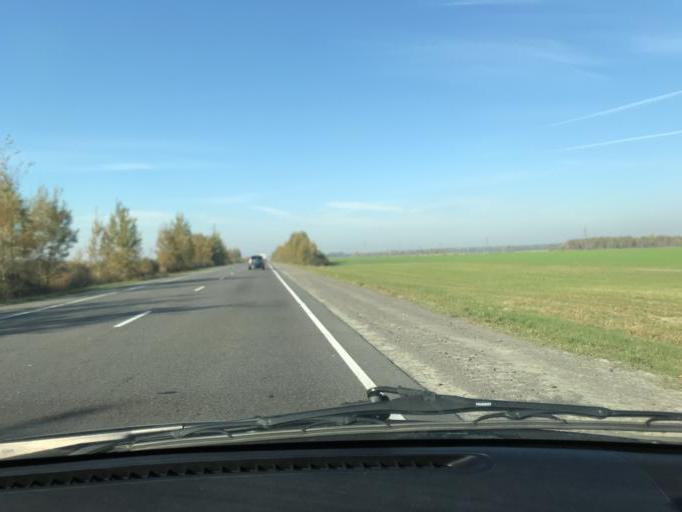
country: BY
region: Brest
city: Horad Luninyets
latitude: 52.3115
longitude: 26.6651
